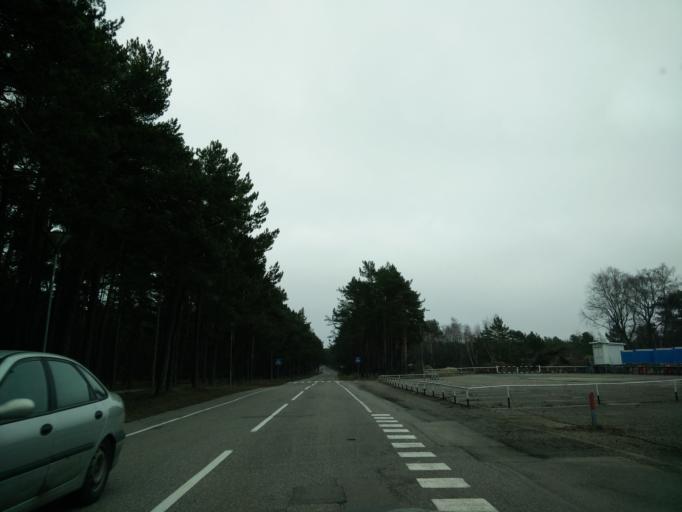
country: LT
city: Nida
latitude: 55.3011
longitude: 20.9866
